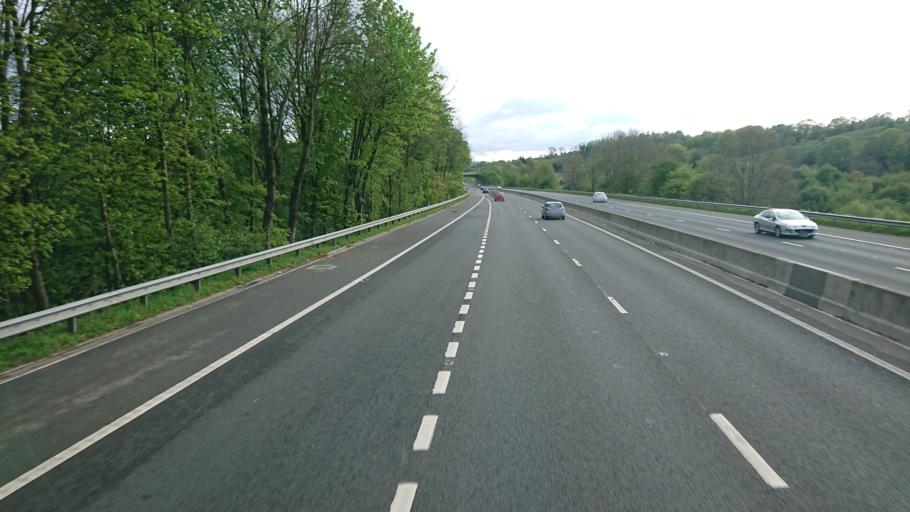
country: GB
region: England
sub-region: Lancashire
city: Brierfield
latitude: 53.8274
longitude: -2.2409
